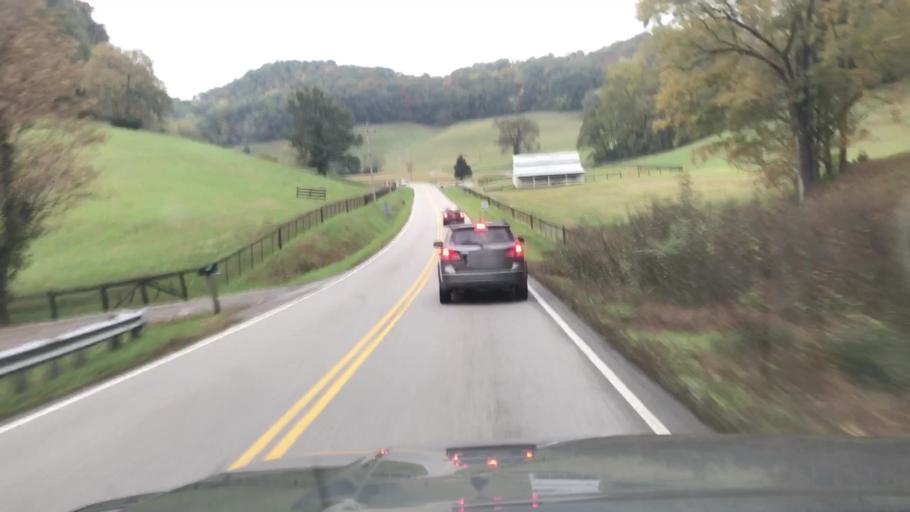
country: US
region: Tennessee
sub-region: Williamson County
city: Brentwood Estates
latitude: 35.9947
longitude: -86.8289
